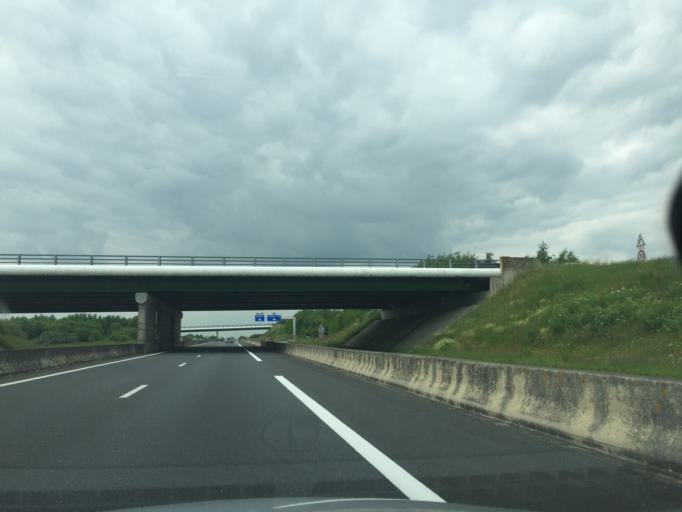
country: FR
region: Pays de la Loire
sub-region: Departement de la Vendee
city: Les Essarts
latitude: 46.8077
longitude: -1.2075
